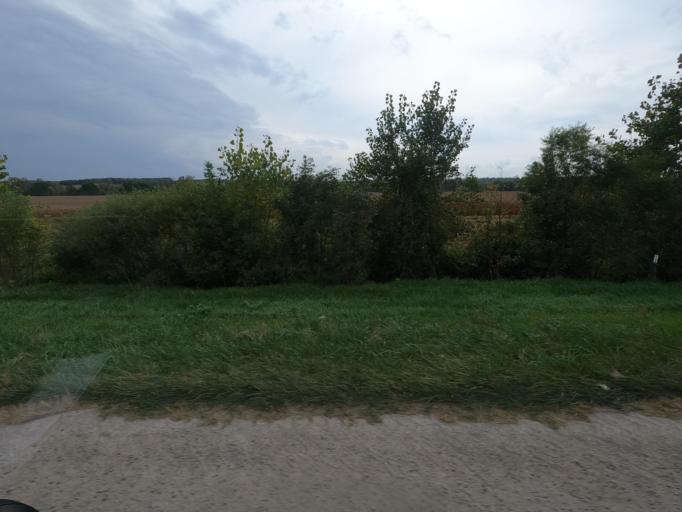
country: US
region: Iowa
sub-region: Van Buren County
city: Keosauqua
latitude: 40.8586
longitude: -92.1253
